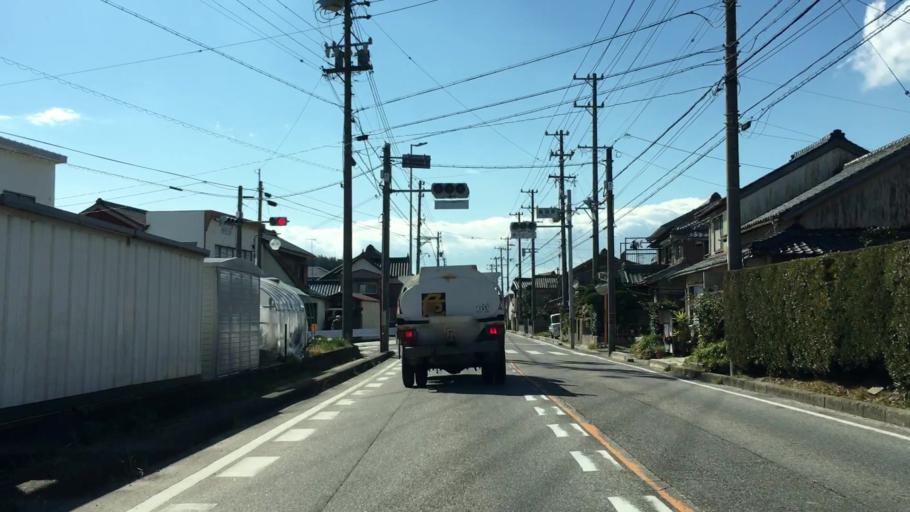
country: JP
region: Aichi
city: Ishiki
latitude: 34.7947
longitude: 137.1081
